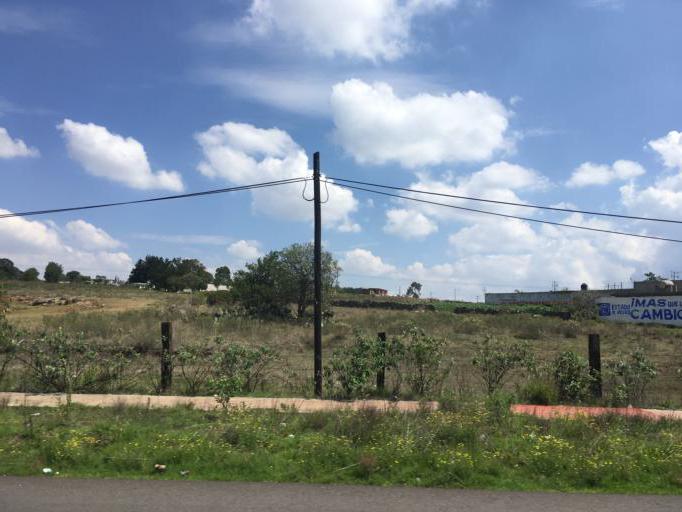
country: MX
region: Mexico
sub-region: Jilotepec
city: Doxhicho
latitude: 19.8931
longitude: -99.6249
